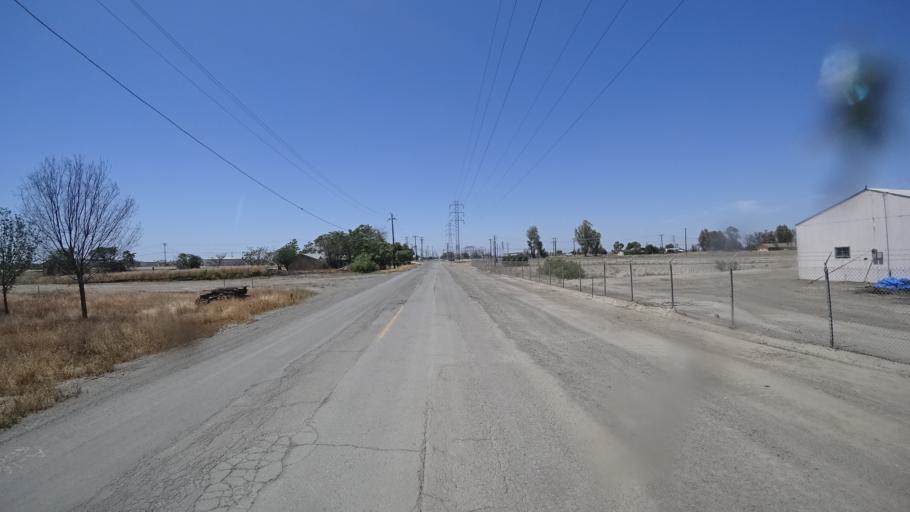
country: US
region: California
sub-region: Kings County
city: Corcoran
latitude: 36.1090
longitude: -119.5519
